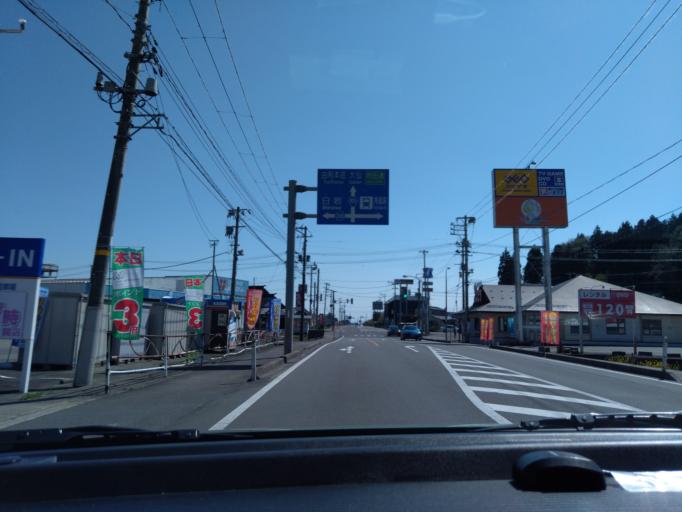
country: JP
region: Akita
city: Kakunodatemachi
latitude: 39.5871
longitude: 140.5719
